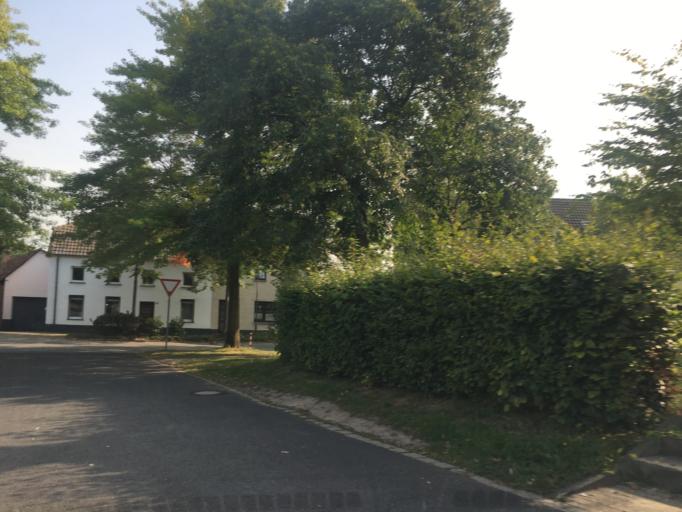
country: DE
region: North Rhine-Westphalia
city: Huckelhoven
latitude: 51.0945
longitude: 6.2179
